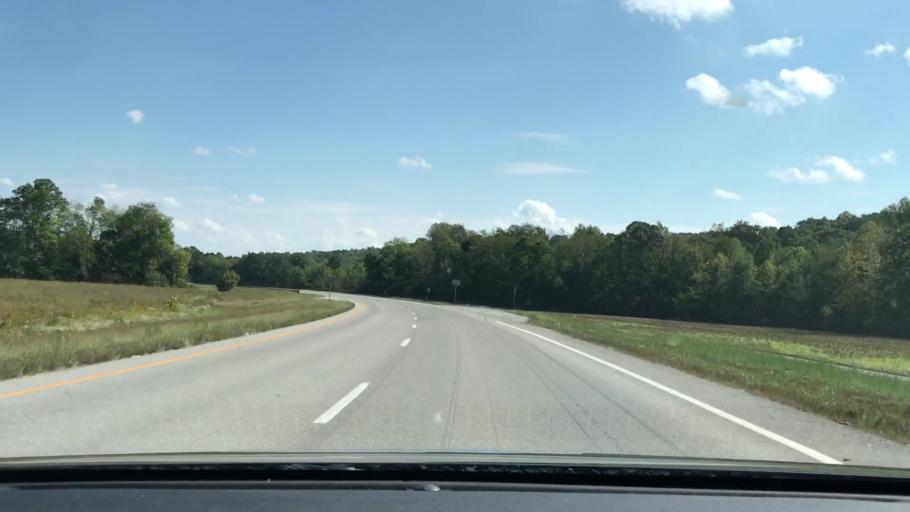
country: US
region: Kentucky
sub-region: Trigg County
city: Cadiz
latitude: 36.7844
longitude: -88.0201
